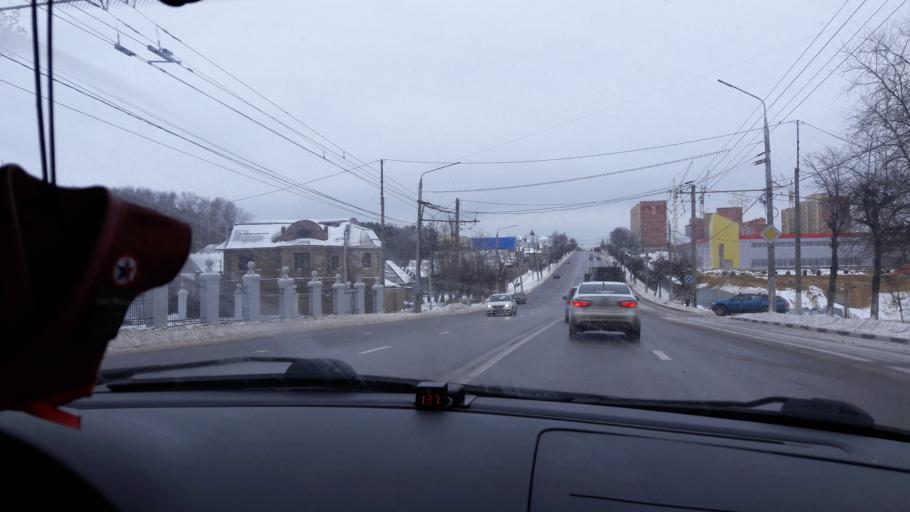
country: RU
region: Tula
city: Gorelki
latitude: 54.2300
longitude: 37.6269
